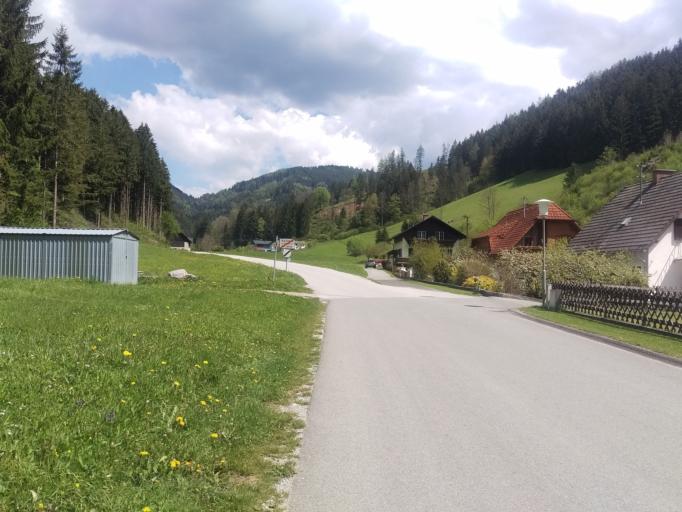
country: AT
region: Styria
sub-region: Politischer Bezirk Bruck-Muerzzuschlag
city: Allerheiligen im Muerztal
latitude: 47.3975
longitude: 15.4344
